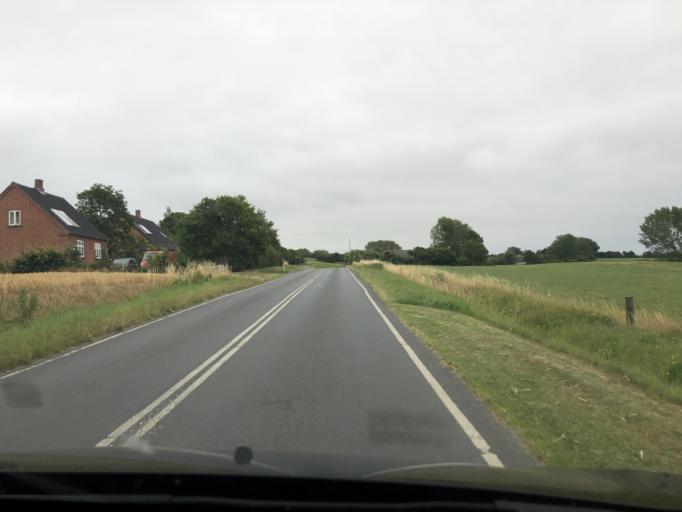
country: DK
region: South Denmark
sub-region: AEro Kommune
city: AEroskobing
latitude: 54.9055
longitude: 10.2948
